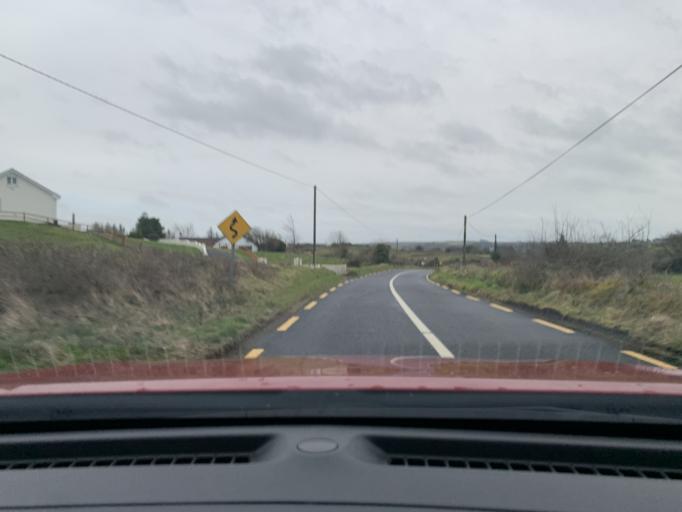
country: IE
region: Connaught
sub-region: Roscommon
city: Boyle
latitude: 53.9782
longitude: -8.3323
